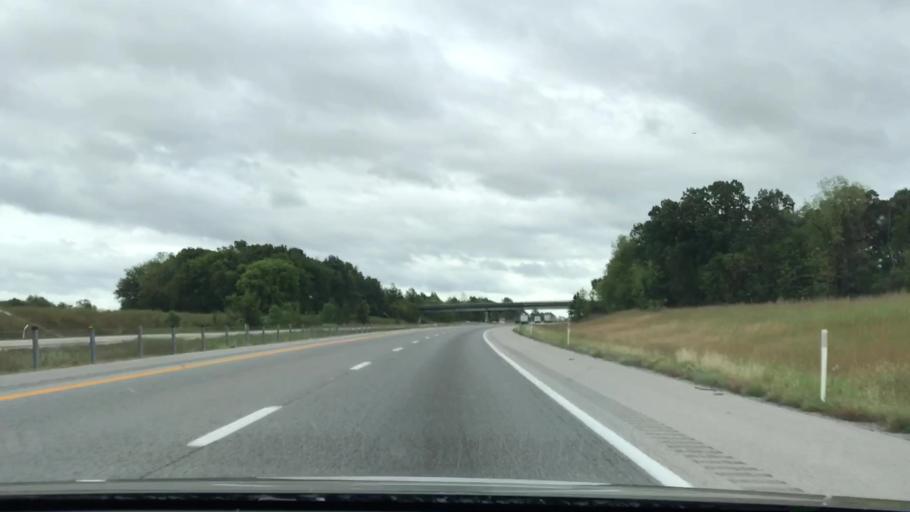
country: US
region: Kentucky
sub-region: Christian County
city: Oak Grove
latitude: 36.7306
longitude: -87.4909
